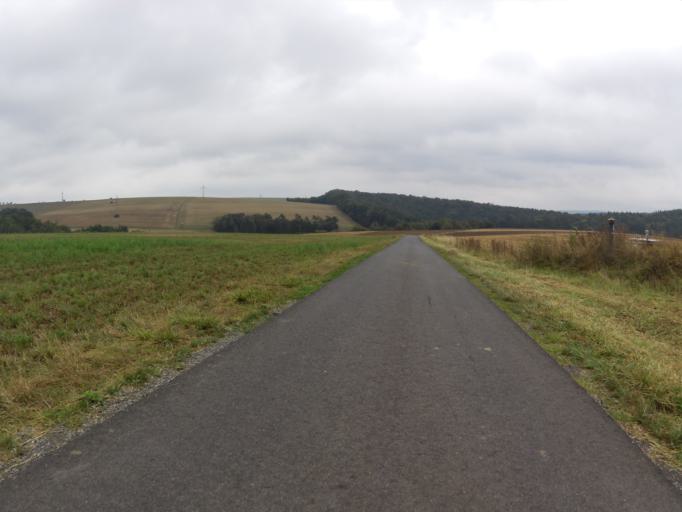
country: DE
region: Bavaria
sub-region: Regierungsbezirk Unterfranken
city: Gadheim
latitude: 49.8503
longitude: 9.9175
